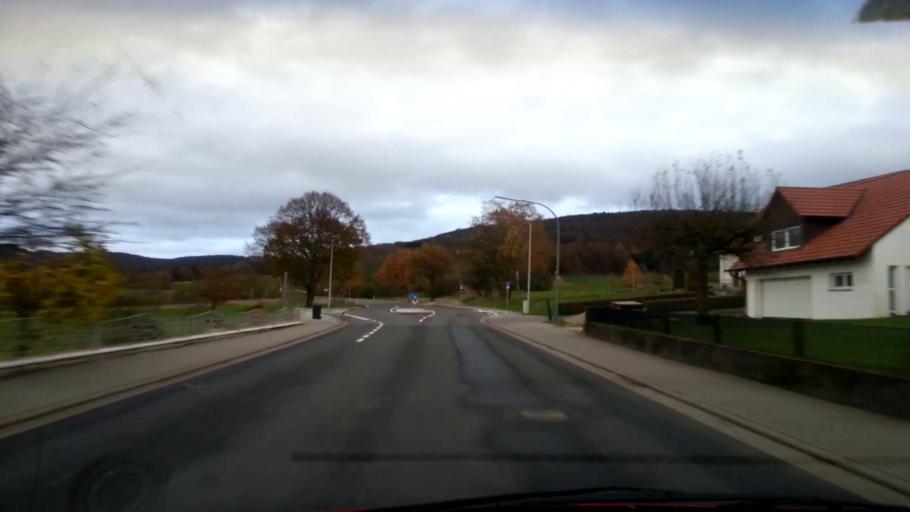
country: DE
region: Bavaria
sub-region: Upper Franconia
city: Litzendorf
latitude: 49.9162
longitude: 11.0508
